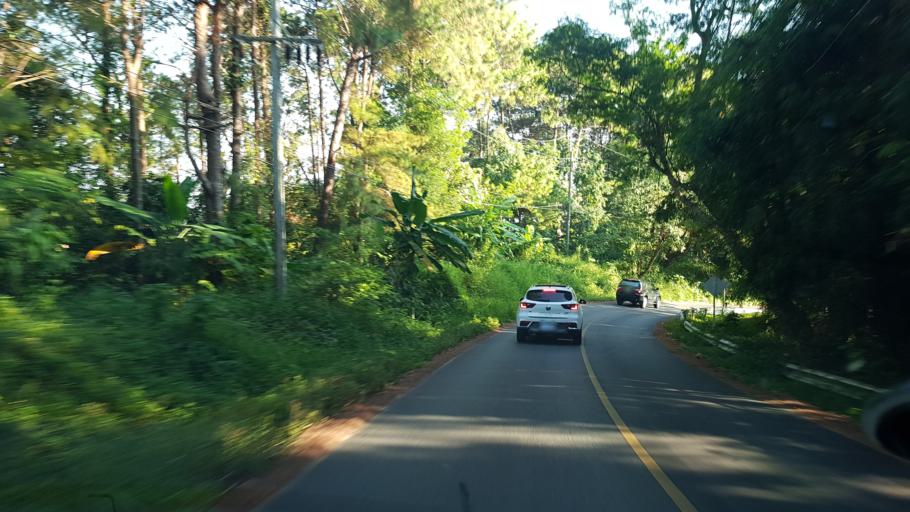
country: TH
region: Chiang Rai
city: Mae Fa Luang
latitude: 20.3129
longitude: 99.8201
